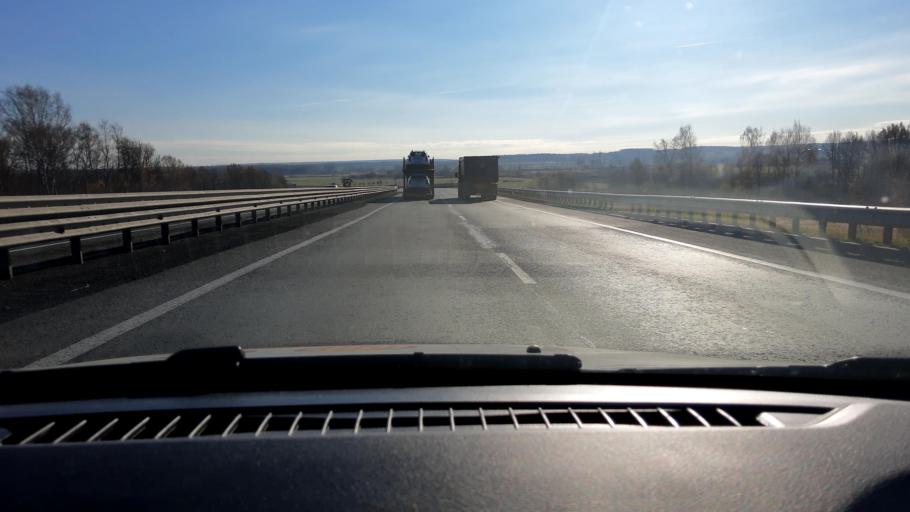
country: RU
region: Nizjnij Novgorod
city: Burevestnik
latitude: 56.1290
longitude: 43.7833
